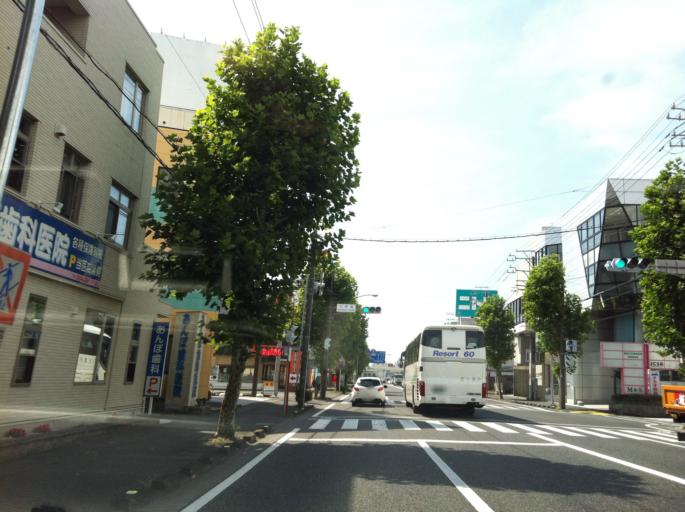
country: JP
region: Shizuoka
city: Shizuoka-shi
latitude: 34.9579
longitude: 138.3804
